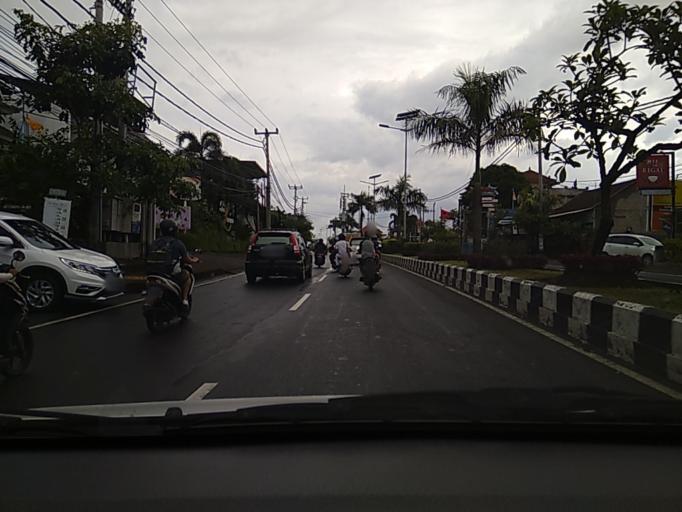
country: ID
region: Bali
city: Bualu
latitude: -8.7858
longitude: 115.2024
